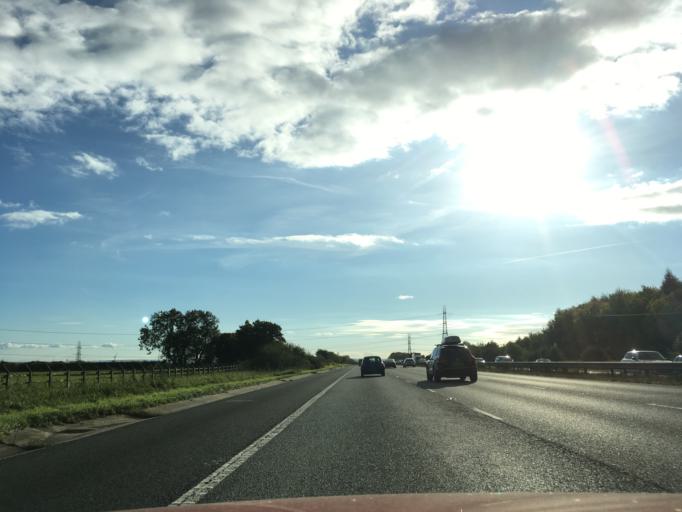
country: GB
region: England
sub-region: South Gloucestershire
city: Tytherington
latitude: 51.5918
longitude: -2.4914
